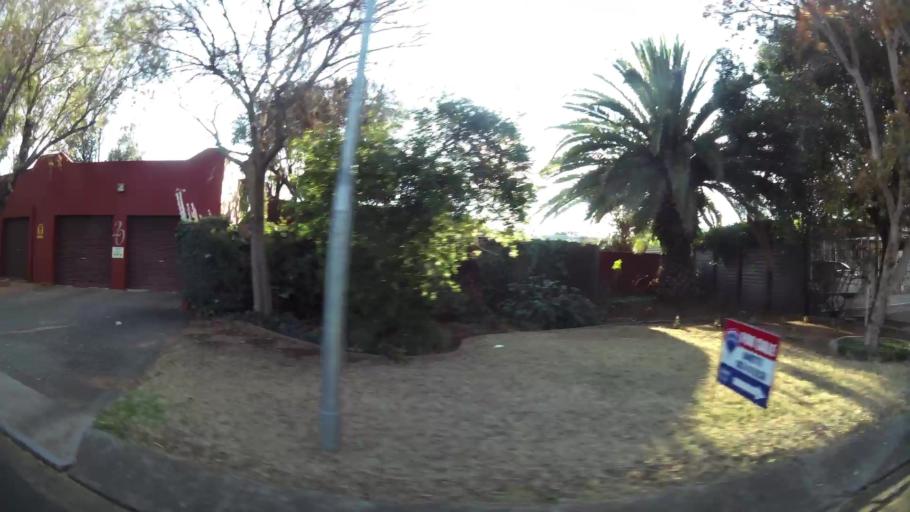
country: ZA
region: Orange Free State
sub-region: Mangaung Metropolitan Municipality
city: Bloemfontein
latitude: -29.1475
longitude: 26.1890
